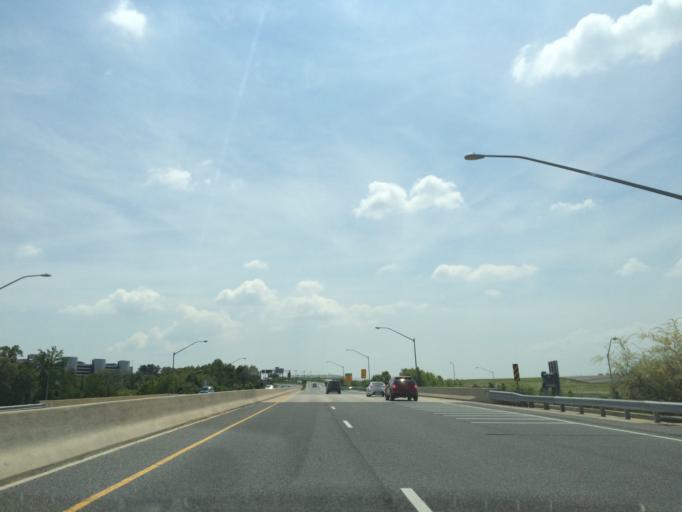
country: US
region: Maryland
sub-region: Anne Arundel County
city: Linthicum
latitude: 39.1890
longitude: -76.6840
